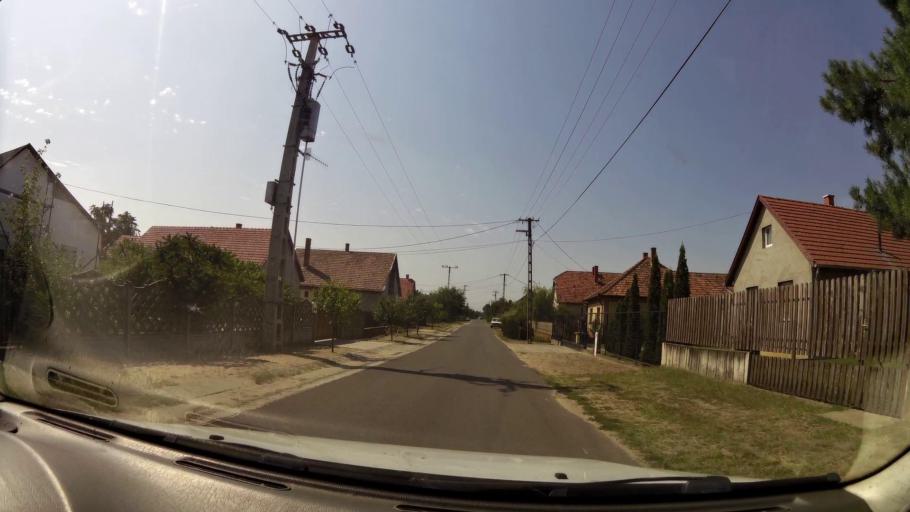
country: HU
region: Pest
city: Ujszilvas
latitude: 47.2672
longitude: 19.9179
